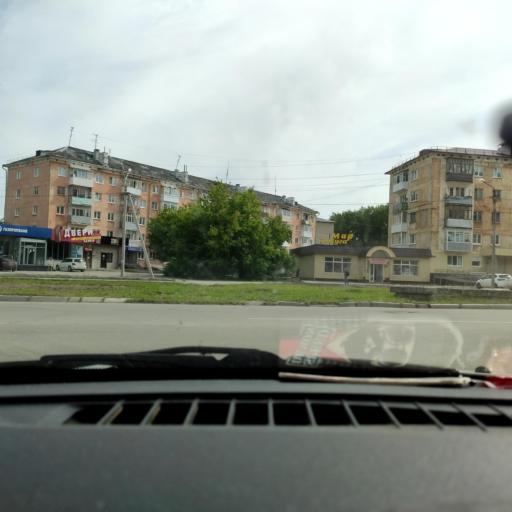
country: RU
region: Perm
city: Chusovoy
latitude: 58.2725
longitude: 57.8109
